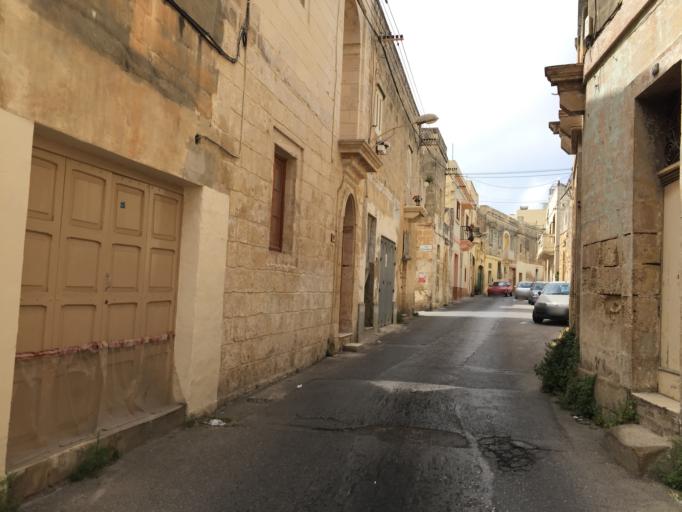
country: MT
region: Haz-Zabbar
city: Zabbar
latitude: 35.8738
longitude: 14.5386
